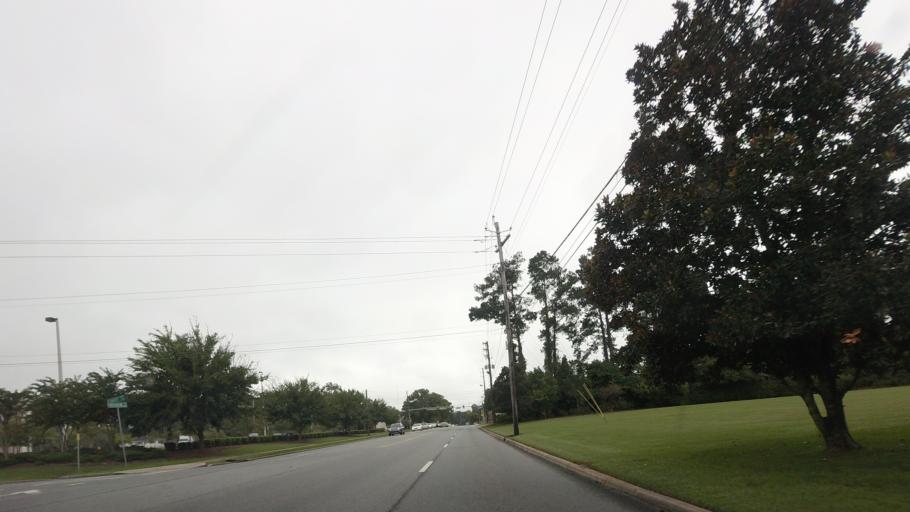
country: US
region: Georgia
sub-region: Lowndes County
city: Remerton
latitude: 30.8611
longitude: -83.2889
